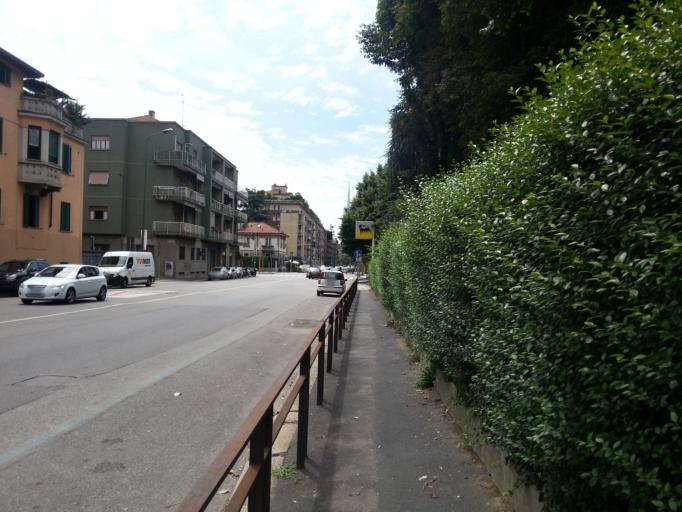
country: IT
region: Lombardy
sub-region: Citta metropolitana di Milano
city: Milano
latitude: 45.4960
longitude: 9.1966
